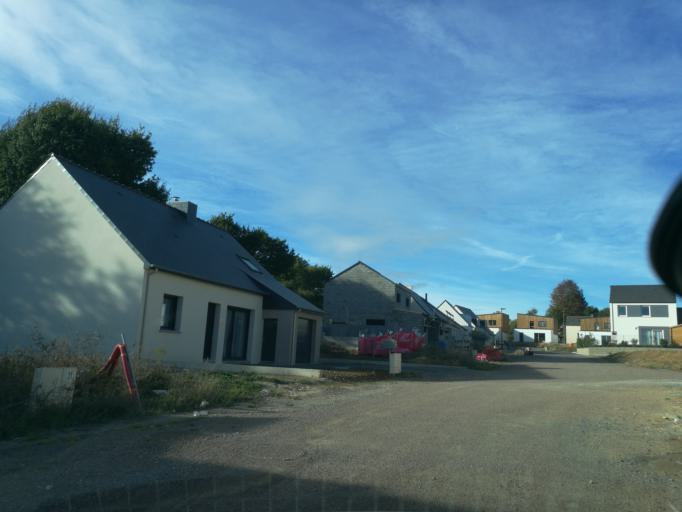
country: FR
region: Brittany
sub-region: Departement d'Ille-et-Vilaine
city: Montauban-de-Bretagne
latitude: 48.1980
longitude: -2.0373
